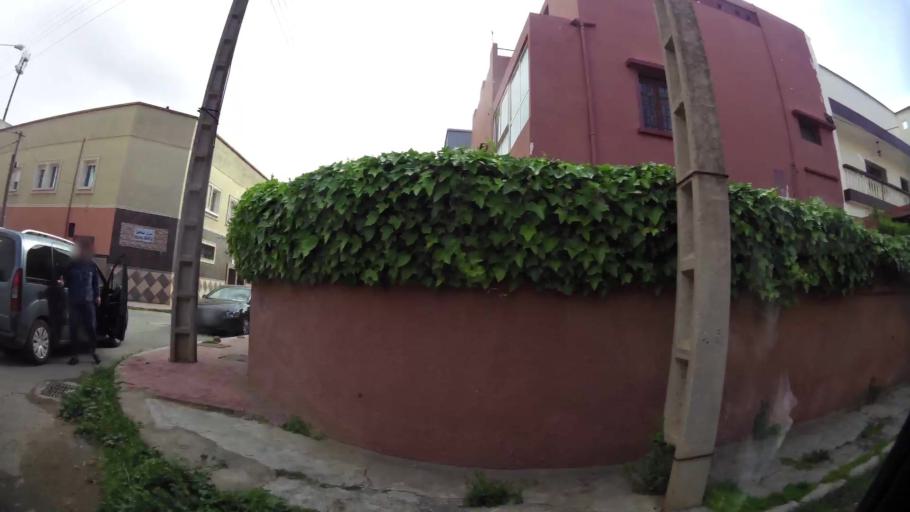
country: MA
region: Doukkala-Abda
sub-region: El-Jadida
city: El Jadida
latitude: 33.2439
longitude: -8.4974
